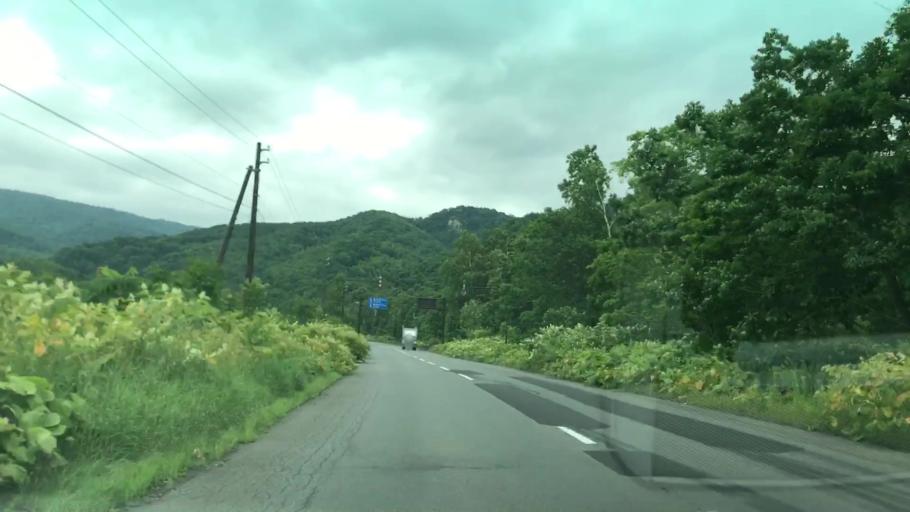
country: JP
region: Hokkaido
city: Yoichi
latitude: 43.0134
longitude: 140.8681
